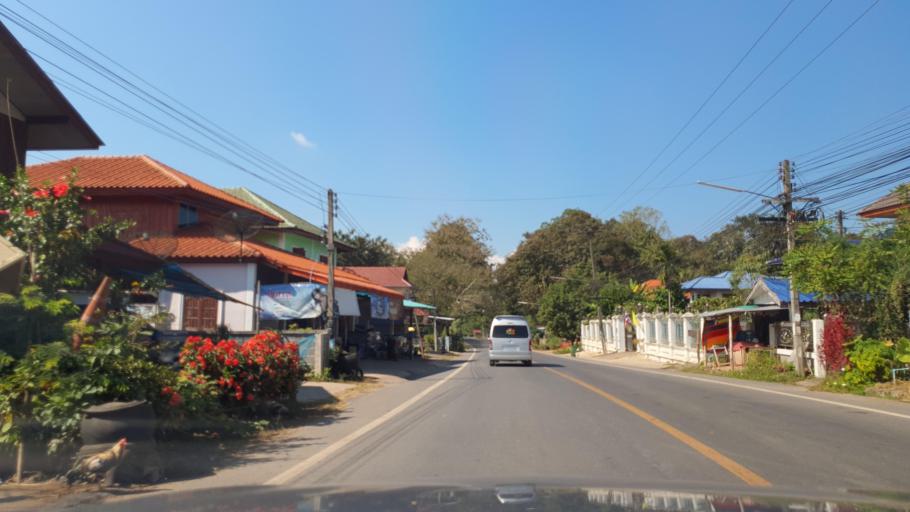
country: TH
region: Nan
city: Tha Wang Pha
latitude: 19.0763
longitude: 100.8655
